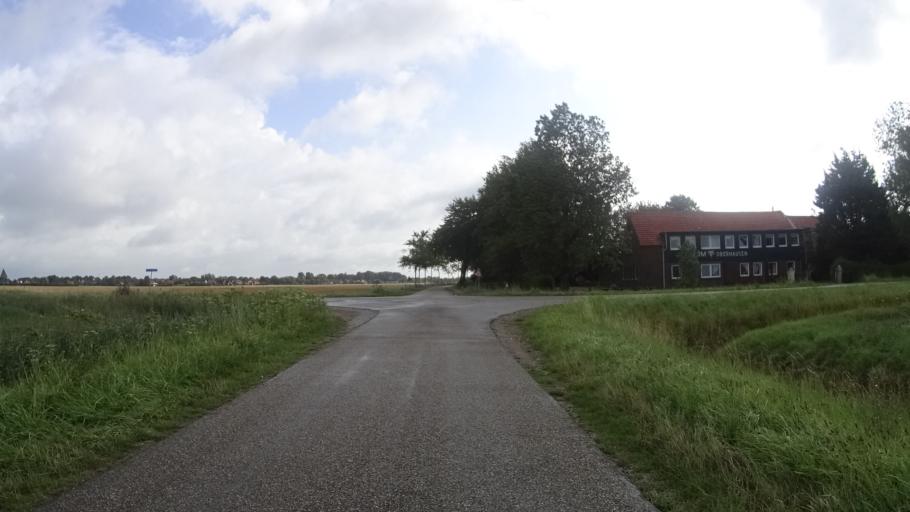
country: NL
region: Zeeland
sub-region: Schouwen-Duiveland
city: Scharendijke
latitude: 51.7224
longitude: 3.8102
